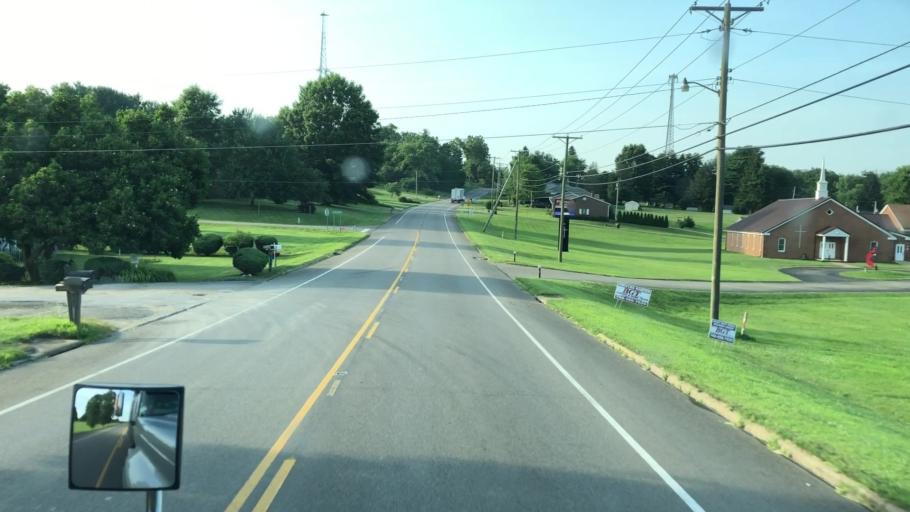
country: US
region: Ohio
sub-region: Muskingum County
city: Pleasant Grove
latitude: 39.9550
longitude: -81.9599
